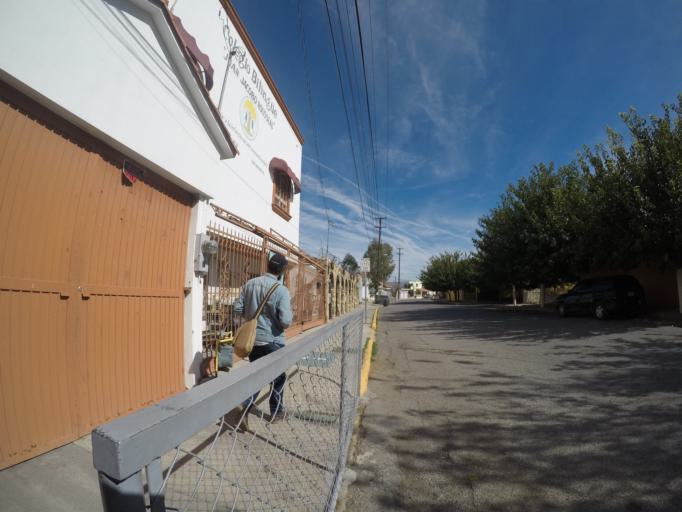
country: MX
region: Chihuahua
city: Ciudad Juarez
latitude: 31.7351
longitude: -106.4392
